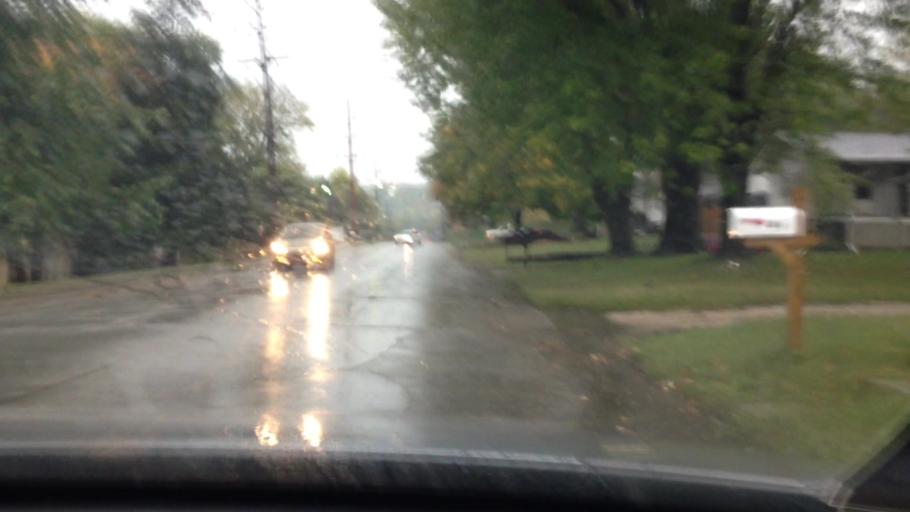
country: US
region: Kansas
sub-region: Leavenworth County
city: Leavenworth
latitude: 39.2959
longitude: -94.9197
